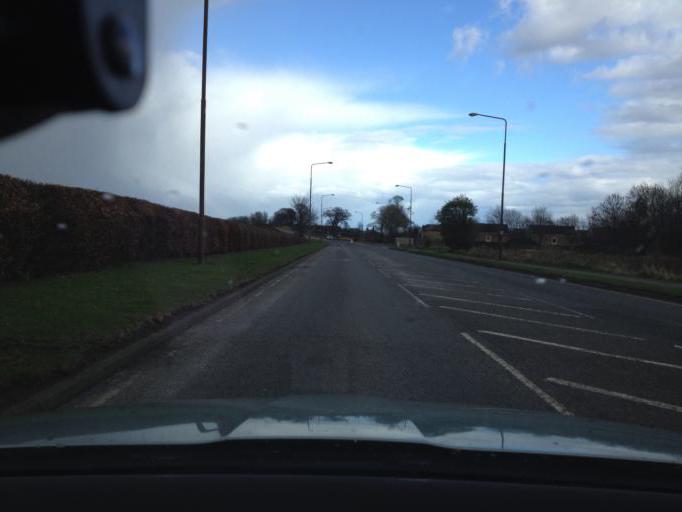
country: GB
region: Scotland
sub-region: West Lothian
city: Linlithgow
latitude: 55.9846
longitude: -3.5770
